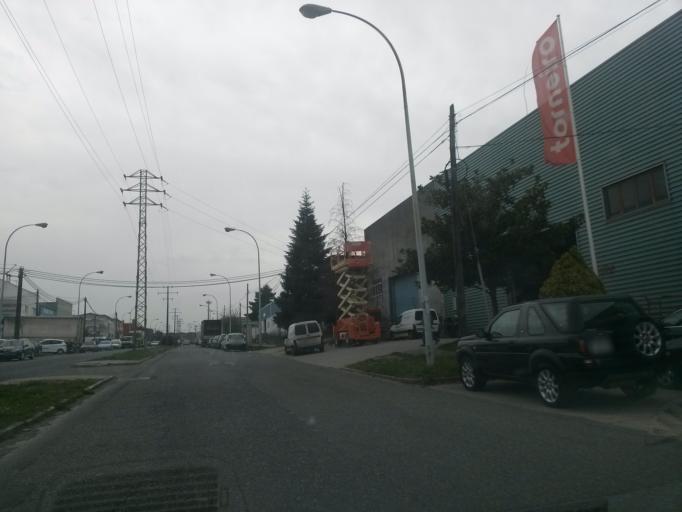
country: ES
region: Galicia
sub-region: Provincia de Lugo
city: Lugo
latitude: 43.0447
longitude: -7.5632
